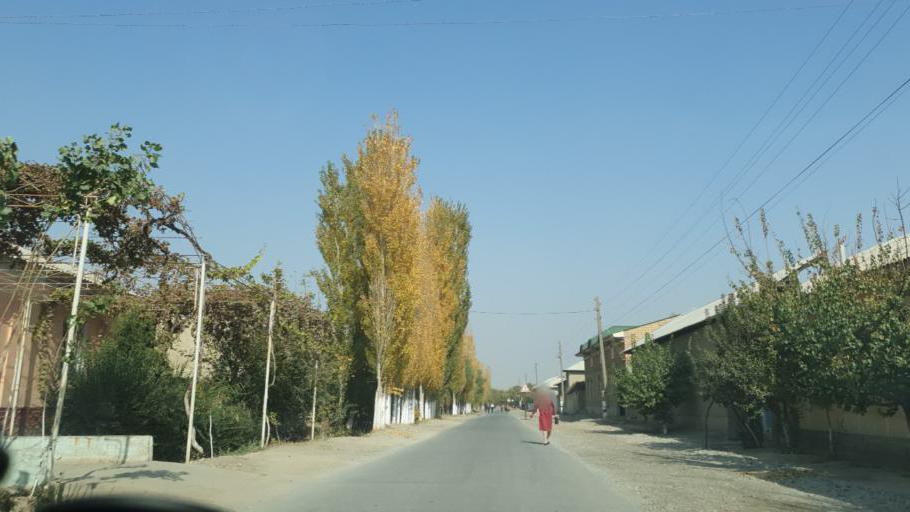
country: UZ
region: Fergana
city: Beshariq
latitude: 40.4925
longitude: 70.6211
